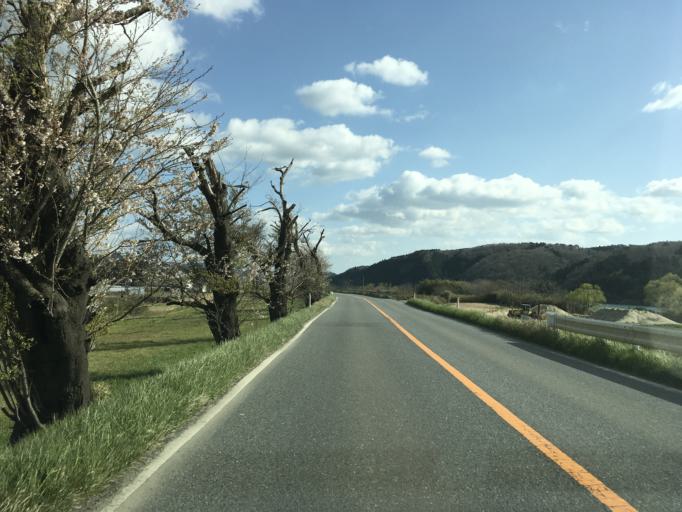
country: JP
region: Miyagi
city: Wakuya
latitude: 38.6444
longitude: 141.2867
